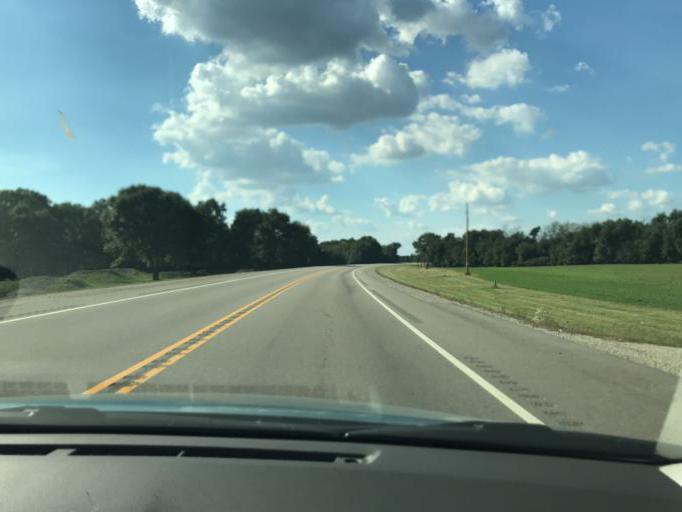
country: US
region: Wisconsin
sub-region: Green County
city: Brodhead
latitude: 42.5759
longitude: -89.3719
